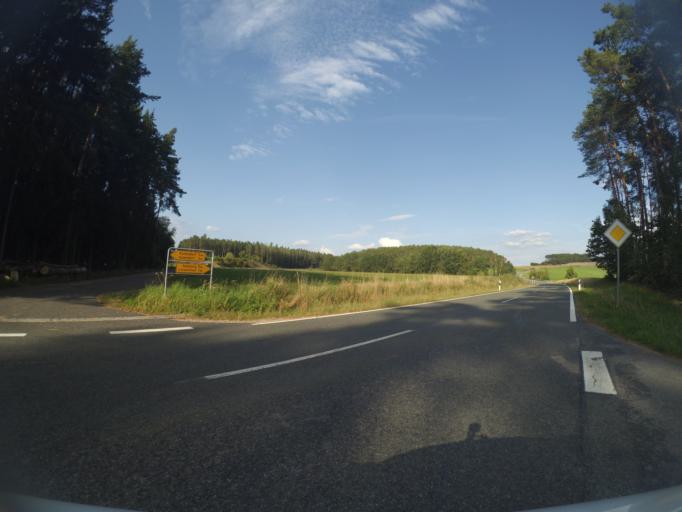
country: DE
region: Bavaria
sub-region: Upper Palatinate
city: Stulln
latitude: 49.4480
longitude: 12.1148
